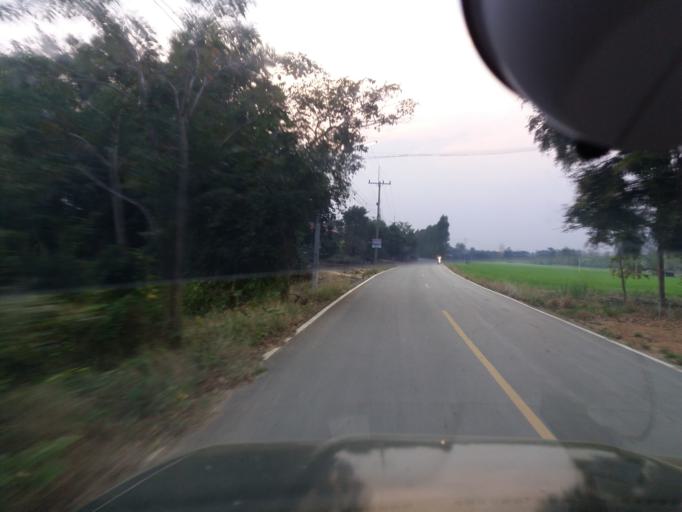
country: TH
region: Suphan Buri
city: Doem Bang Nang Buat
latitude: 14.8930
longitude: 100.1807
